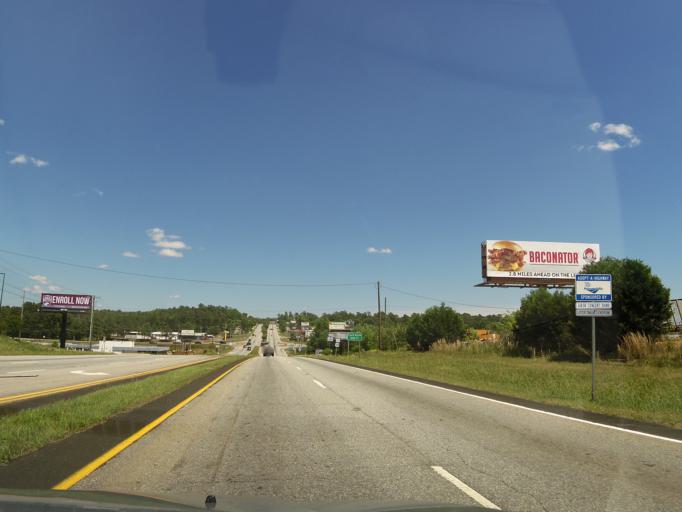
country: US
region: South Carolina
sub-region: Aiken County
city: Warrenville
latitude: 33.5609
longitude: -81.7821
